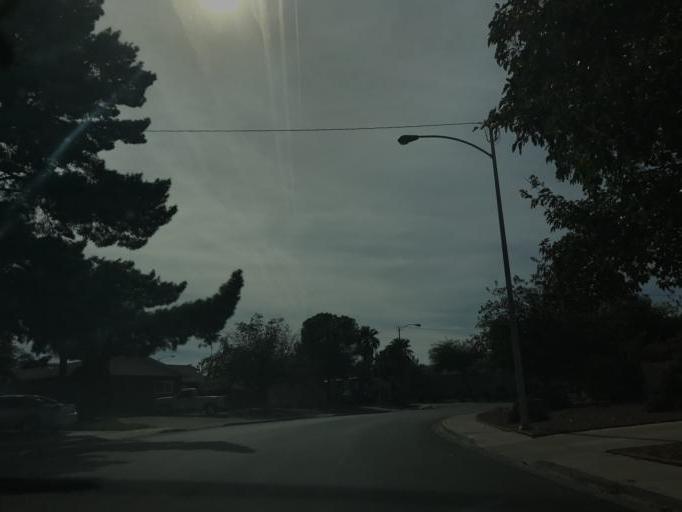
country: US
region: Nevada
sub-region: Clark County
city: Winchester
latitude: 36.1274
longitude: -115.1001
